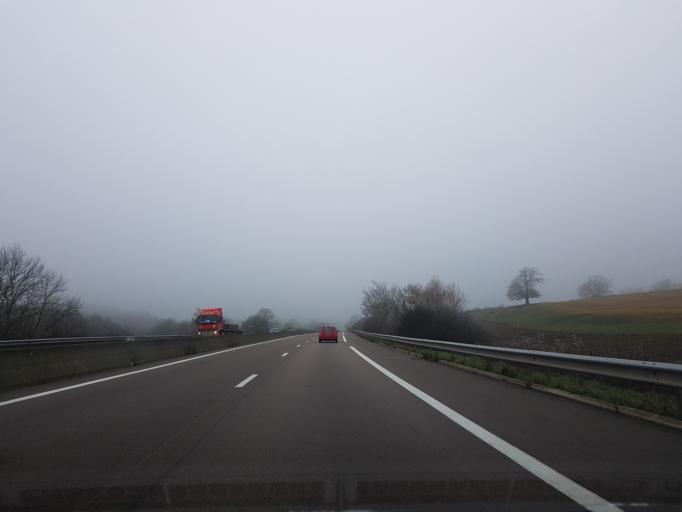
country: FR
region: Bourgogne
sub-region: Departement de Saone-et-Loire
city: Ecuisses
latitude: 46.7444
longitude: 4.5305
